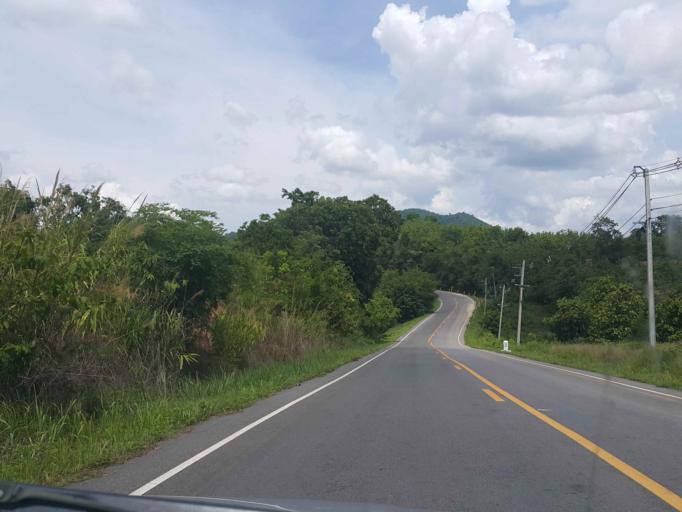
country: TH
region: Nan
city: Ban Luang
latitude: 18.8624
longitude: 100.4586
